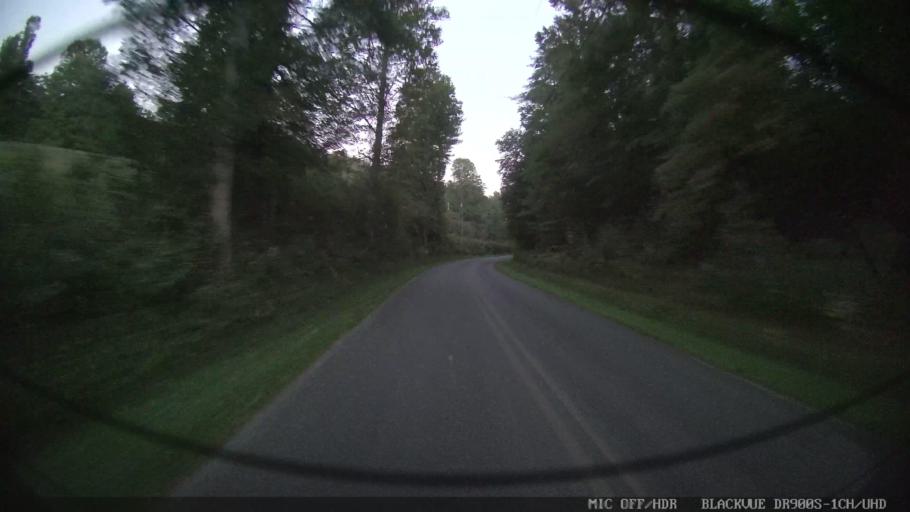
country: US
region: Georgia
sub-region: Gilmer County
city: Ellijay
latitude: 34.7823
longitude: -84.5460
